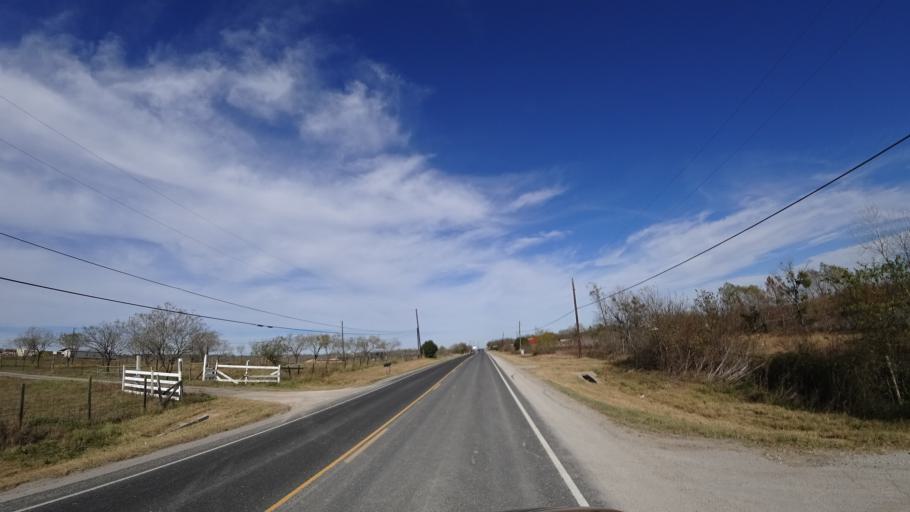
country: US
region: Texas
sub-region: Travis County
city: Onion Creek
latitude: 30.1177
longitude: -97.7172
